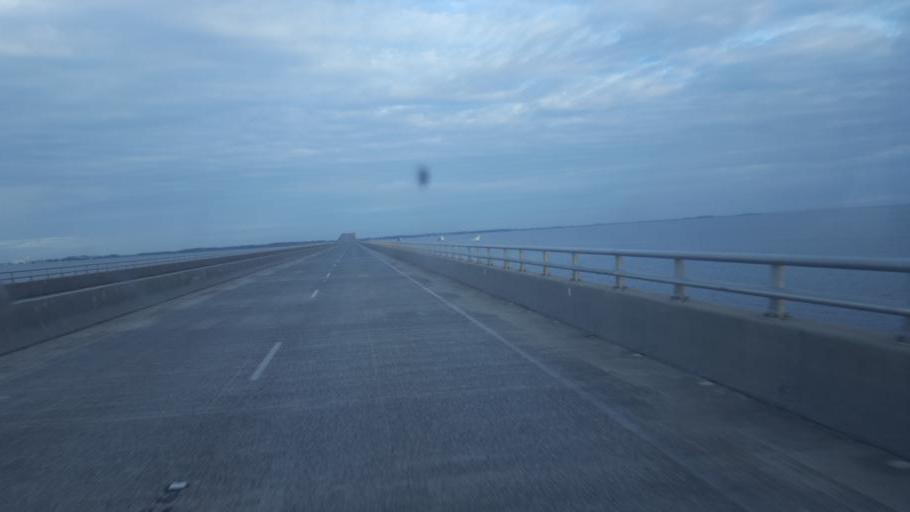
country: US
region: North Carolina
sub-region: Dare County
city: Manteo
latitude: 35.8840
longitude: -75.7025
